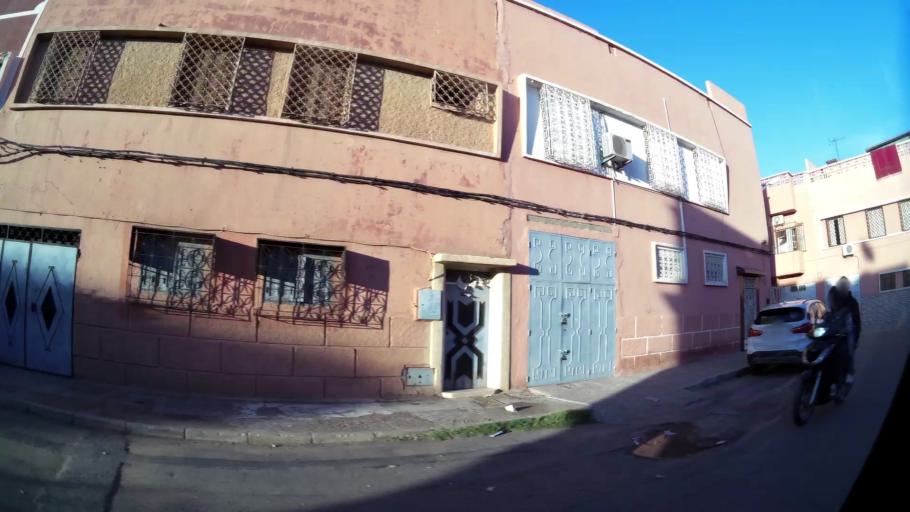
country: MA
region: Marrakech-Tensift-Al Haouz
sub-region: Marrakech
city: Marrakesh
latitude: 31.6246
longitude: -8.0346
